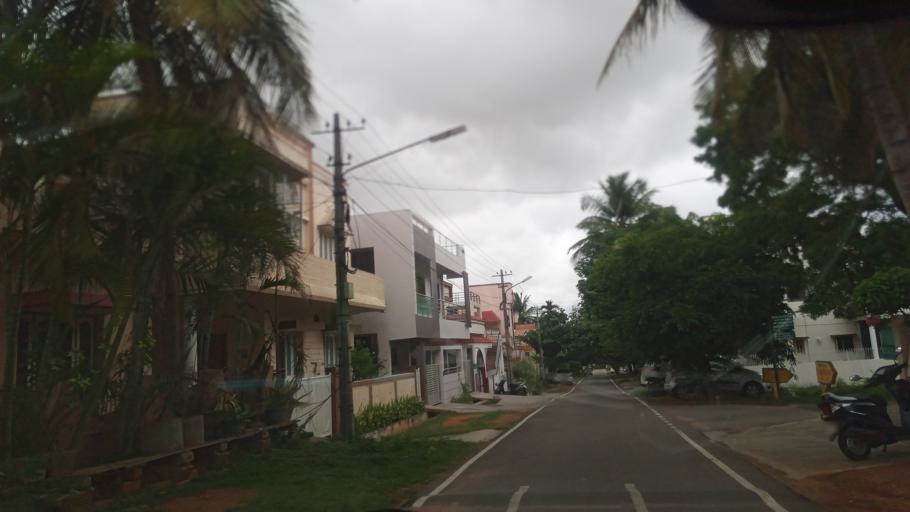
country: IN
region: Karnataka
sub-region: Mysore
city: Mysore
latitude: 12.2889
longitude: 76.6144
